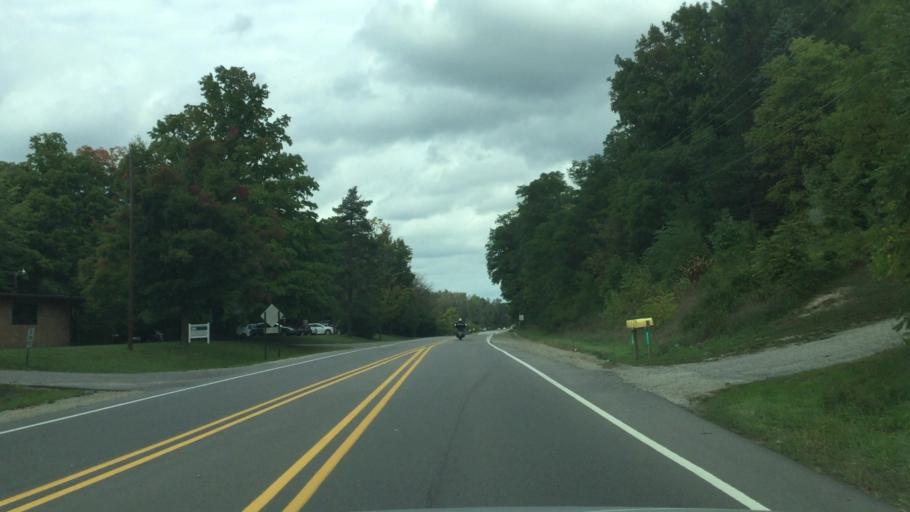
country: US
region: Michigan
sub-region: Livingston County
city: Brighton
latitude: 42.5536
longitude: -83.7533
